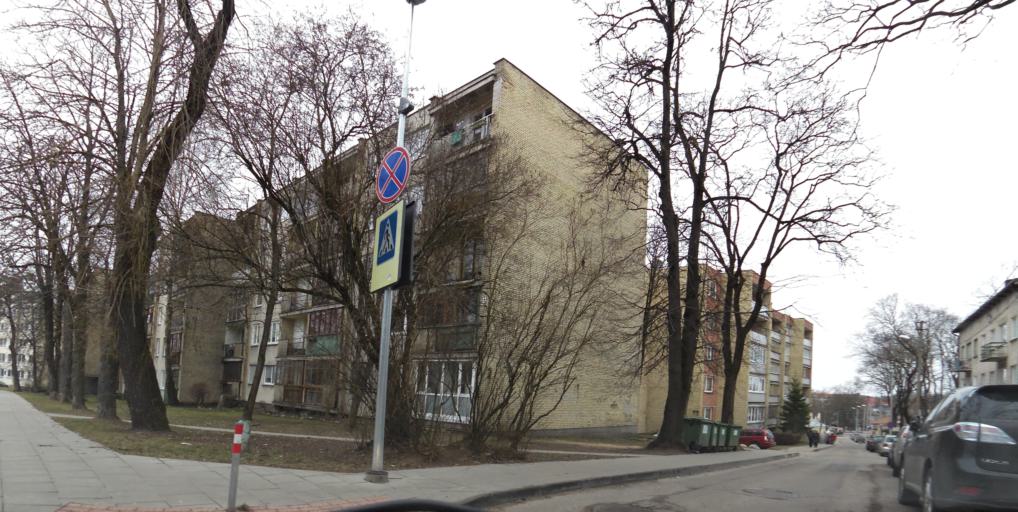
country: LT
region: Vilnius County
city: Naujamiestis
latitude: 54.6786
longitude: 25.2621
